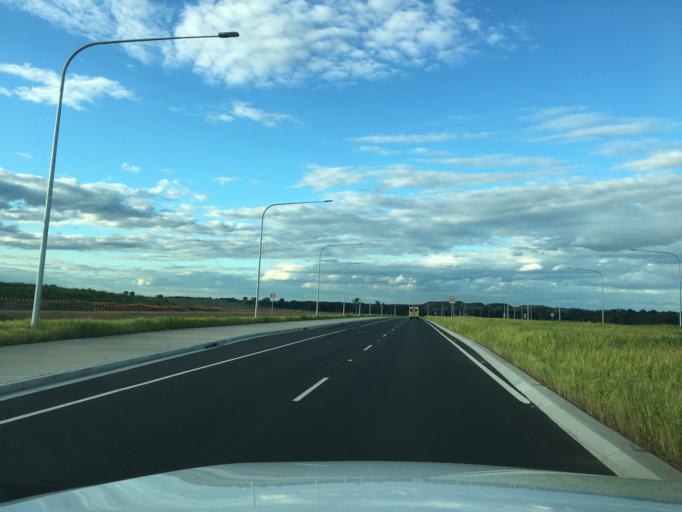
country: AU
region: New South Wales
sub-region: Liverpool
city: Bringelly
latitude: -33.8802
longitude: 150.7453
